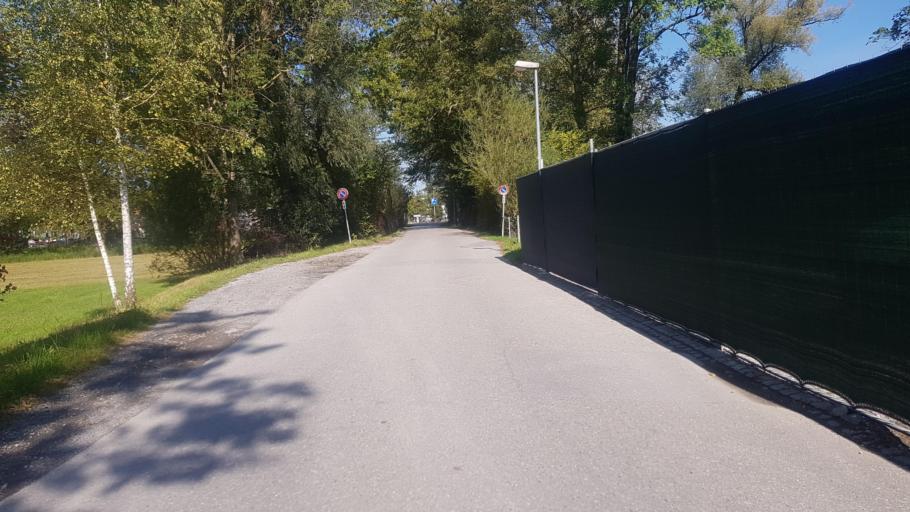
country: CH
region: Saint Gallen
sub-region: Wahlkreis Rheintal
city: Rheineck
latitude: 47.4963
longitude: 9.5611
